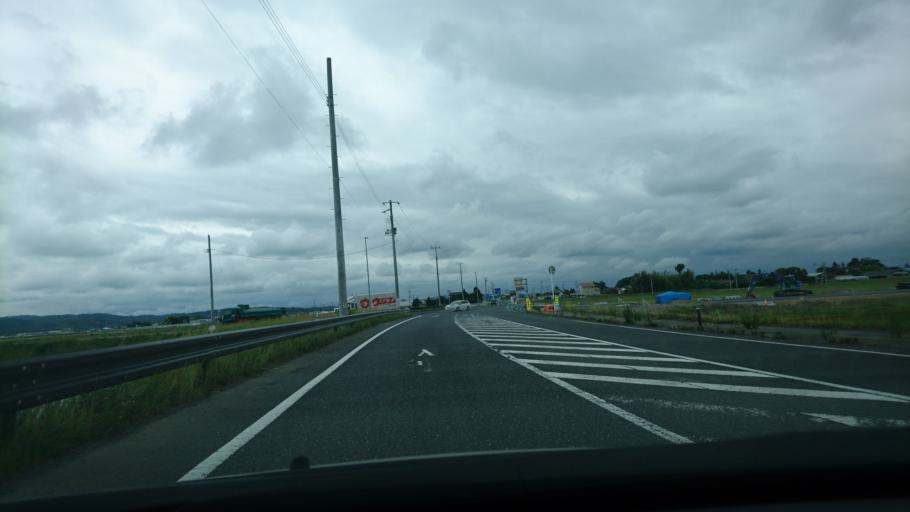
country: JP
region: Miyagi
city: Wakuya
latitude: 38.6784
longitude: 141.2607
